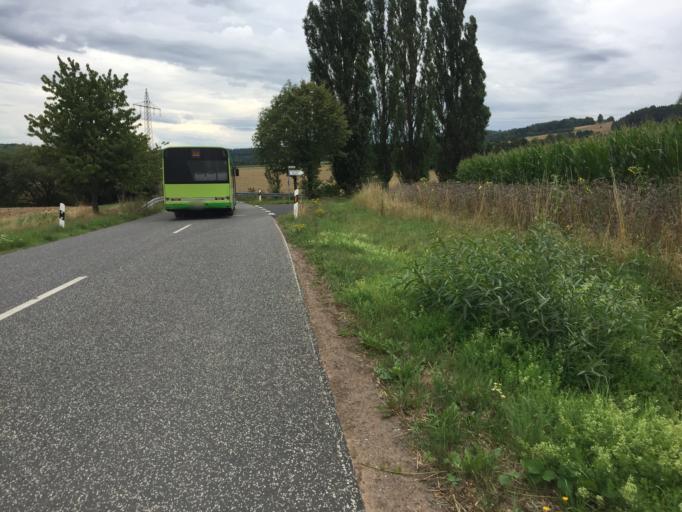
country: DE
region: Hesse
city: Breitenbach
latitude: 50.9171
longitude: 9.7686
